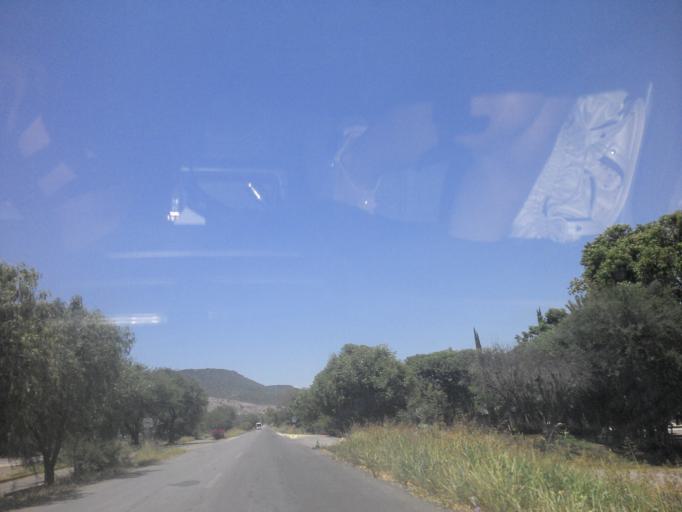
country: MX
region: Guanajuato
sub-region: San Francisco del Rincon
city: San Ignacio de Hidalgo
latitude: 20.9193
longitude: -101.9172
